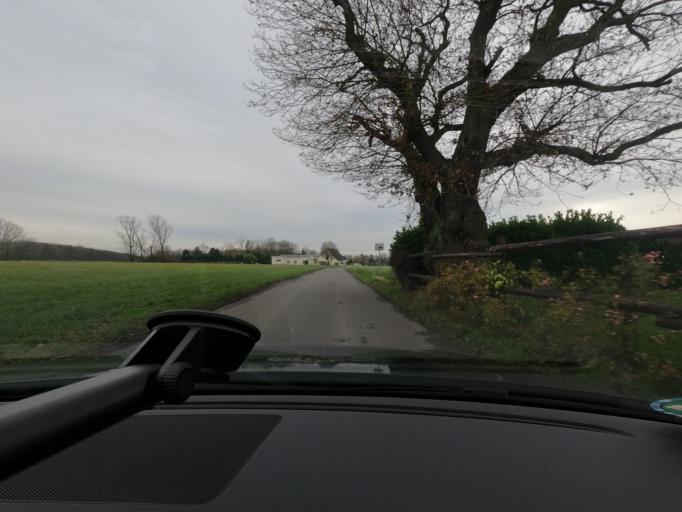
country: DE
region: North Rhine-Westphalia
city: Tonisvorst
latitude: 51.3411
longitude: 6.5206
